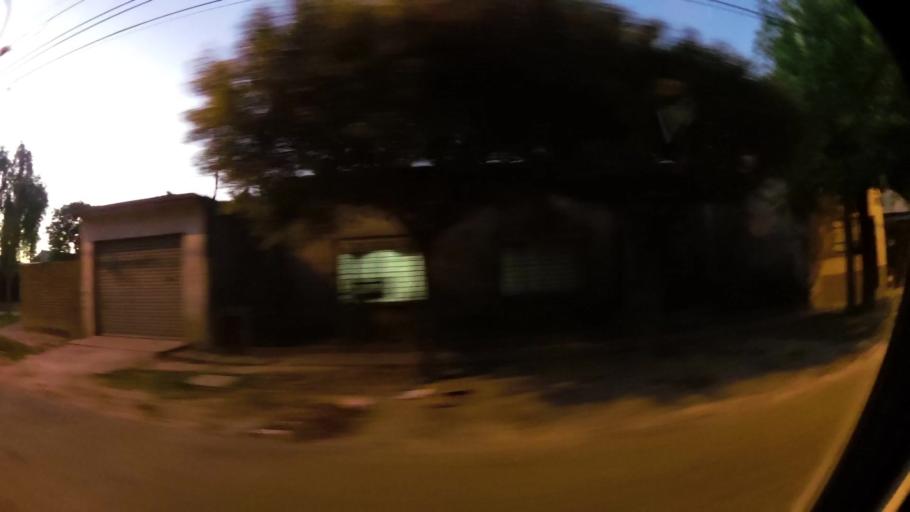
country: AR
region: Buenos Aires
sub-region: Partido de Quilmes
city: Quilmes
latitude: -34.7850
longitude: -58.1856
